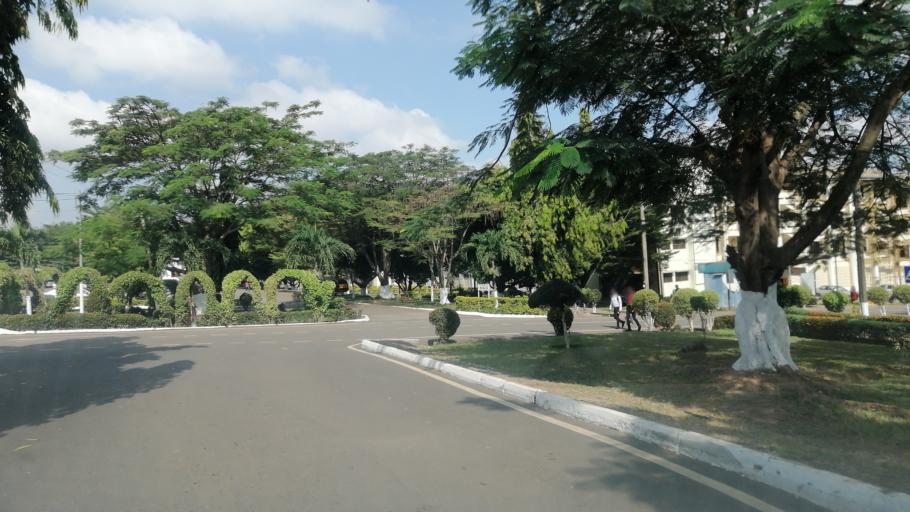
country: GH
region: Ashanti
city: Kumasi
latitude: 6.6970
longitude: -1.6821
